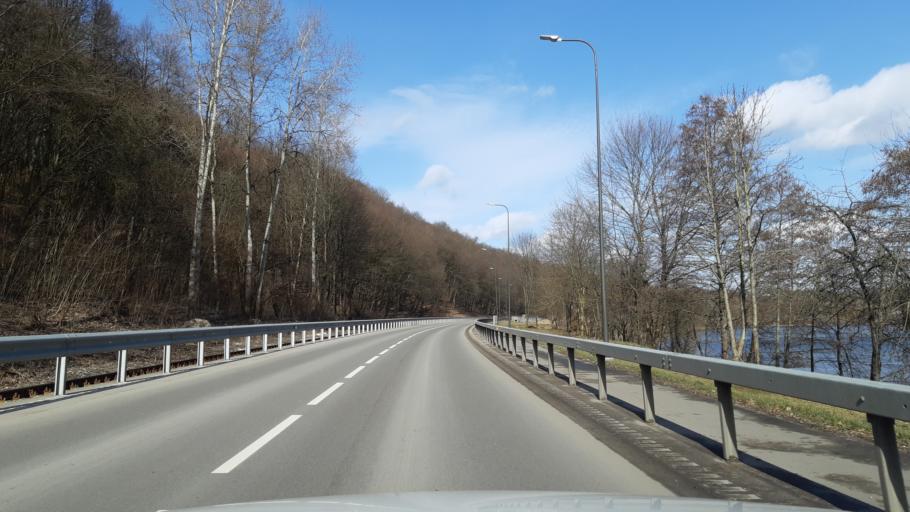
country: LT
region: Kauno apskritis
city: Dainava (Kaunas)
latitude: 54.8832
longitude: 23.9565
